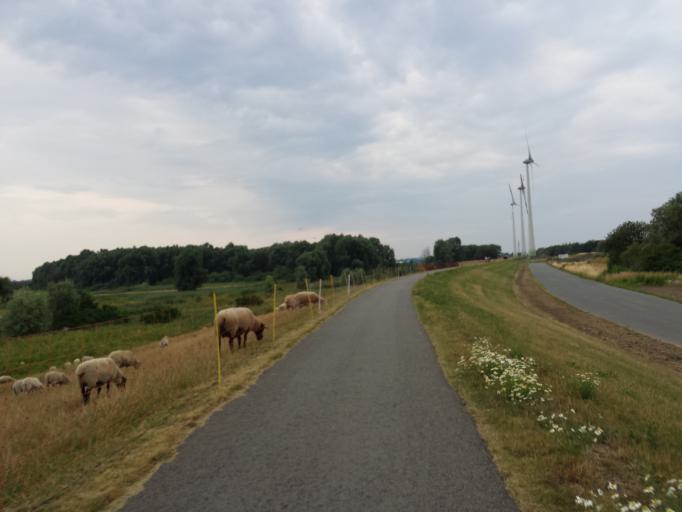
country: DE
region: Lower Saxony
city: Ritterhude
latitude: 53.1091
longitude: 8.7269
